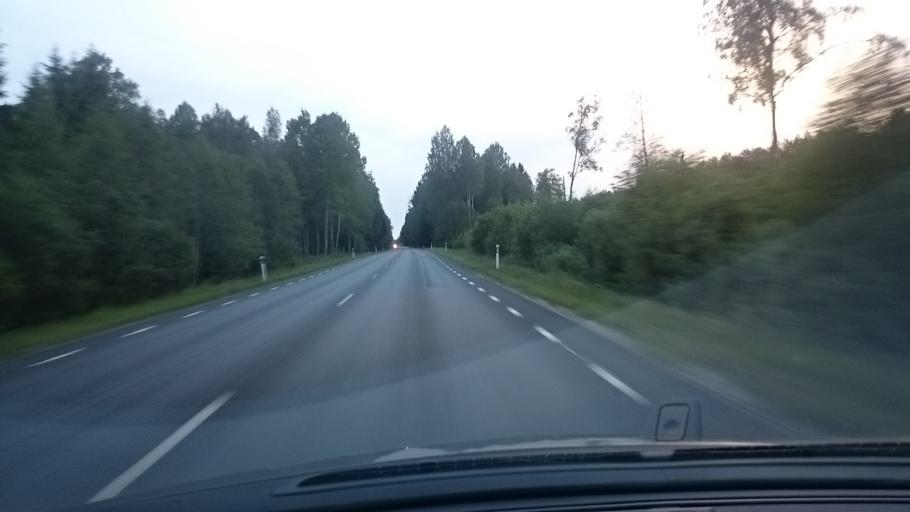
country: EE
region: Raplamaa
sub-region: Kehtna vald
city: Kehtna
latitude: 58.8447
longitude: 25.0497
